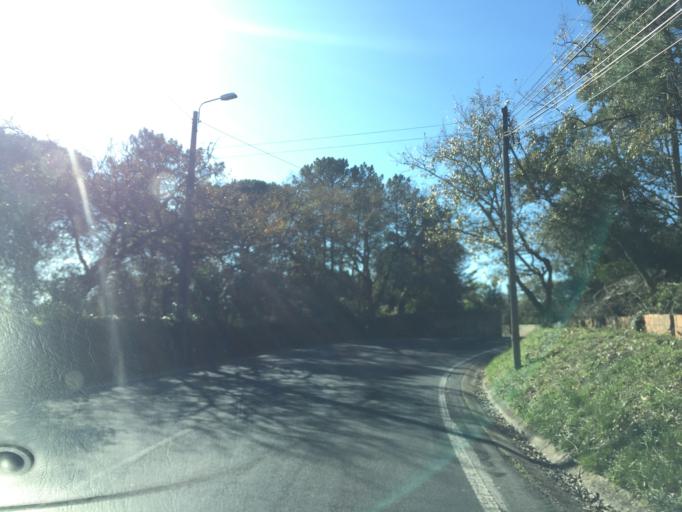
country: PT
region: Lisbon
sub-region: Sintra
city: Belas
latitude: 38.7916
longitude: -9.2669
